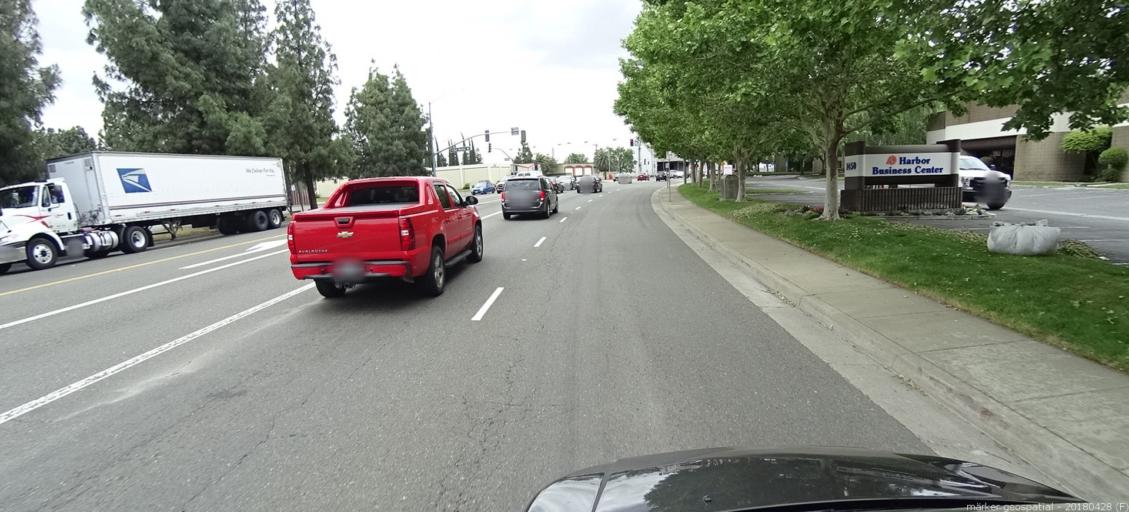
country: US
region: California
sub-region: Yolo County
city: West Sacramento
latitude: 38.5710
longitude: -121.5488
